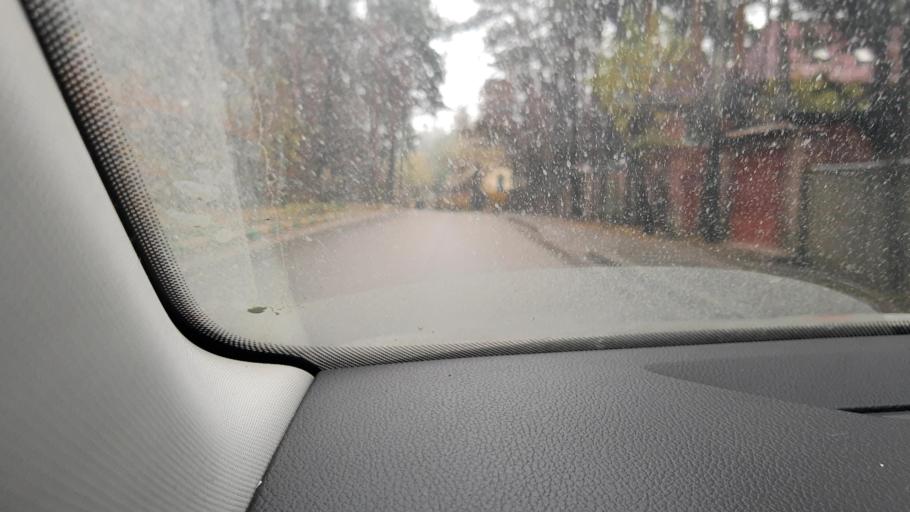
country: RU
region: Moscow
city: Zagor'ye
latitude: 55.5444
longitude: 37.6760
